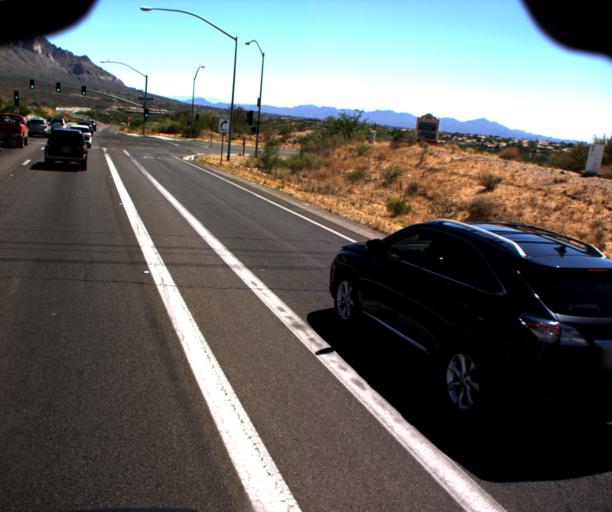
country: US
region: Arizona
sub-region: Pima County
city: Oro Valley
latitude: 32.4276
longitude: -110.9348
